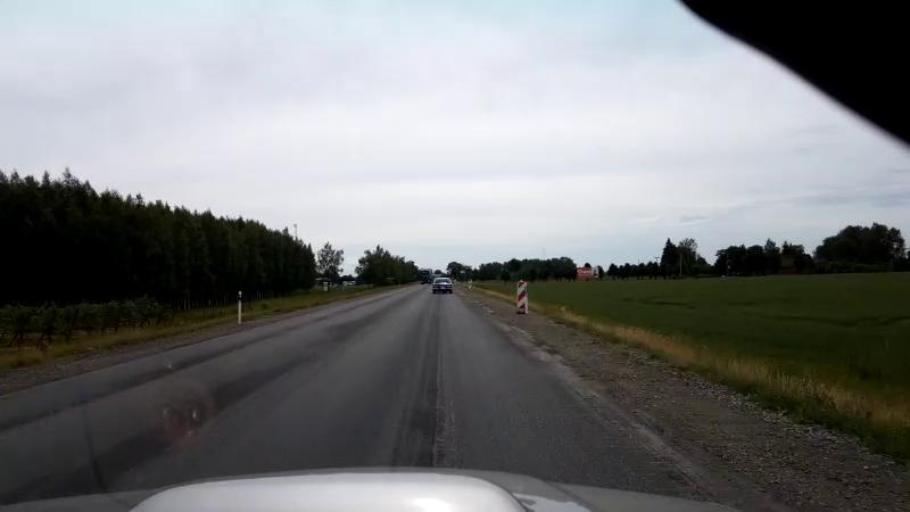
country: LV
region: Bauskas Rajons
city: Bauska
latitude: 56.3673
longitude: 24.2761
